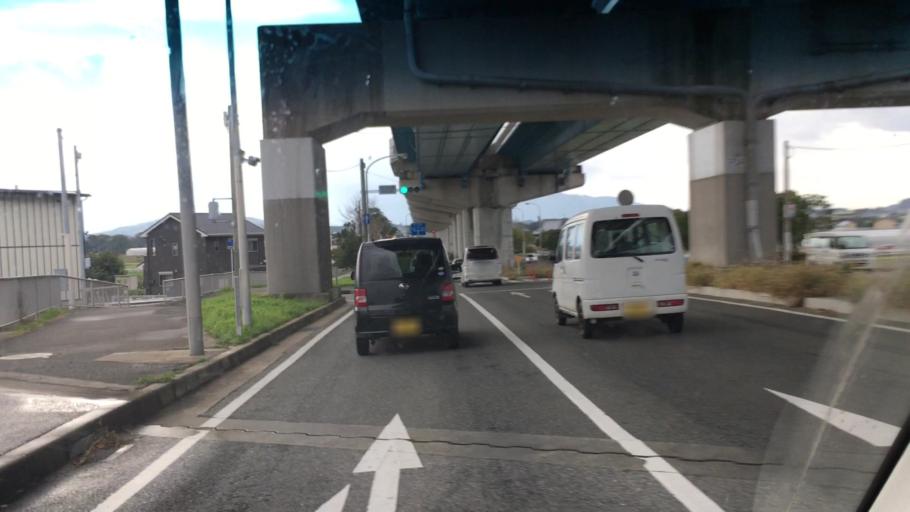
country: JP
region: Fukuoka
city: Maebaru-chuo
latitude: 33.5606
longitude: 130.2324
